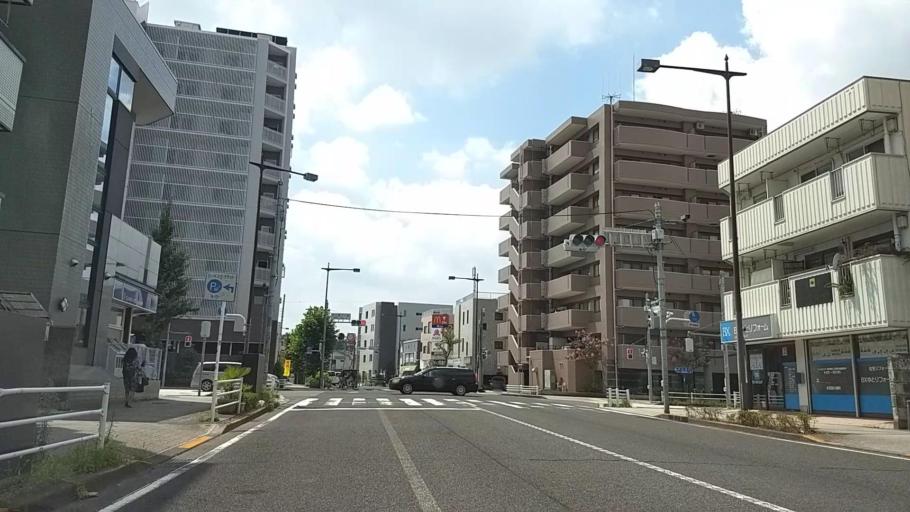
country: JP
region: Tokyo
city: Hachioji
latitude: 35.6550
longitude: 139.3328
